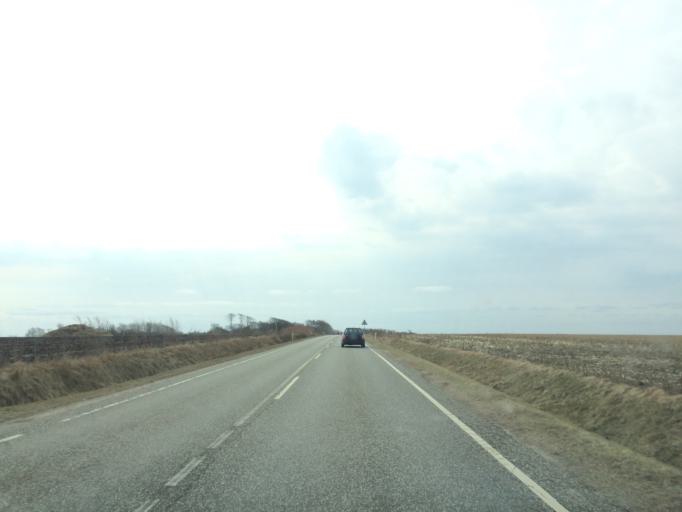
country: DK
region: Central Jutland
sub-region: Ringkobing-Skjern Kommune
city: Skjern
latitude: 56.0260
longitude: 8.5023
